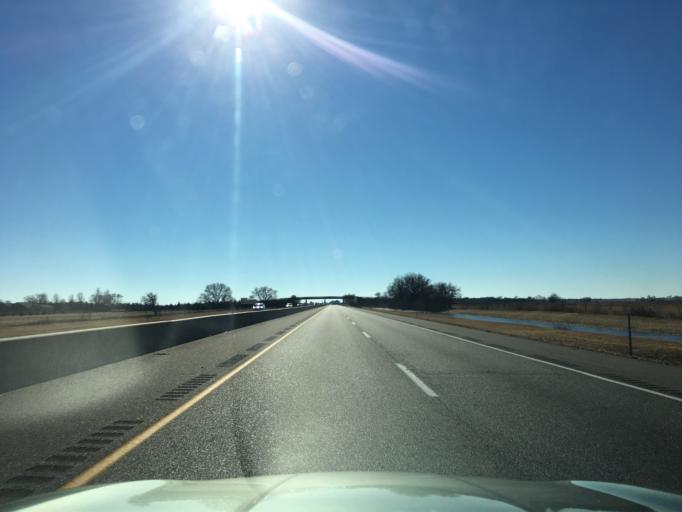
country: US
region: Kansas
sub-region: Sumner County
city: Mulvane
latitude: 37.4688
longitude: -97.3228
